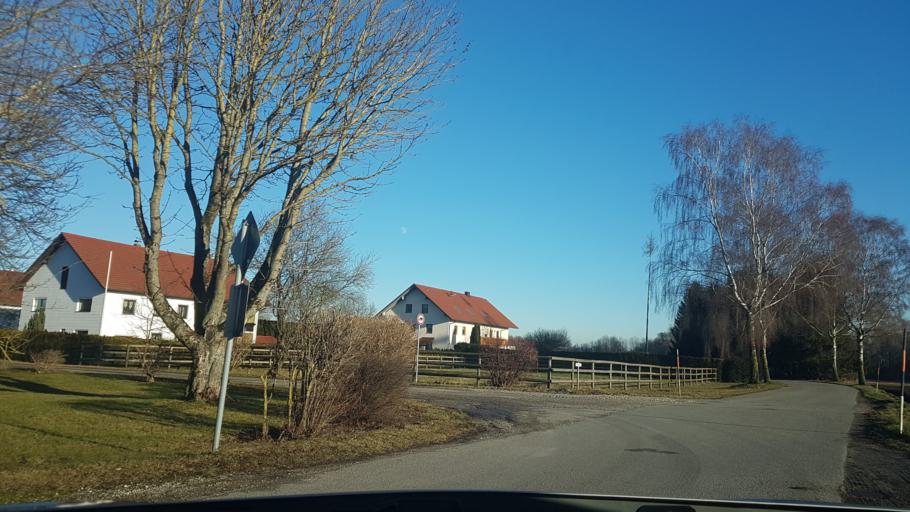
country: DE
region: Bavaria
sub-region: Upper Bavaria
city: Eichenried
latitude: 48.2875
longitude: 11.7863
